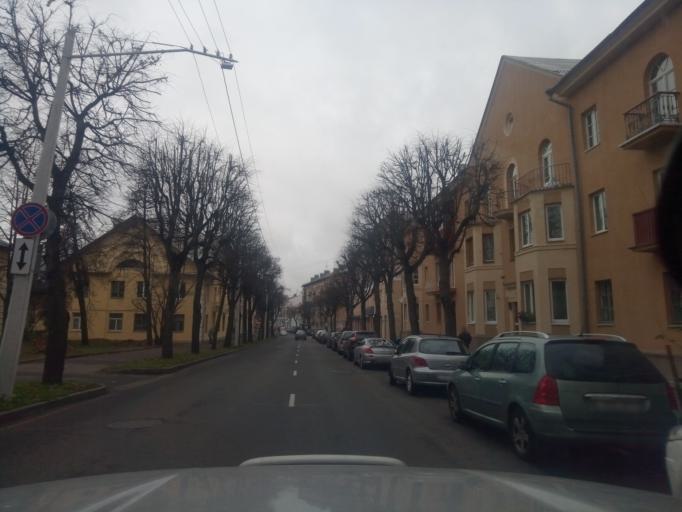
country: BY
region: Minsk
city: Minsk
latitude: 53.9136
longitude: 27.5668
